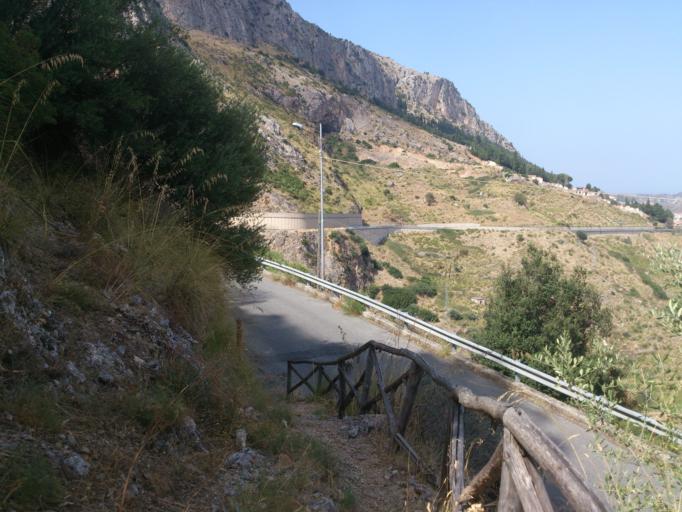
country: IT
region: Calabria
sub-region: Provincia di Reggio Calabria
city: Pazzano
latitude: 38.4699
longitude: 16.4554
